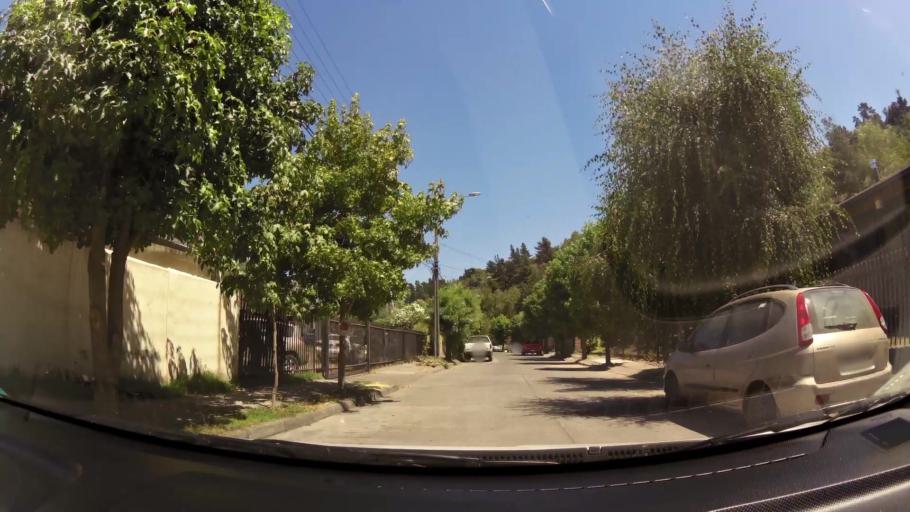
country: CL
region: Maule
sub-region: Provincia de Curico
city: Curico
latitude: -34.9816
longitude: -71.2284
